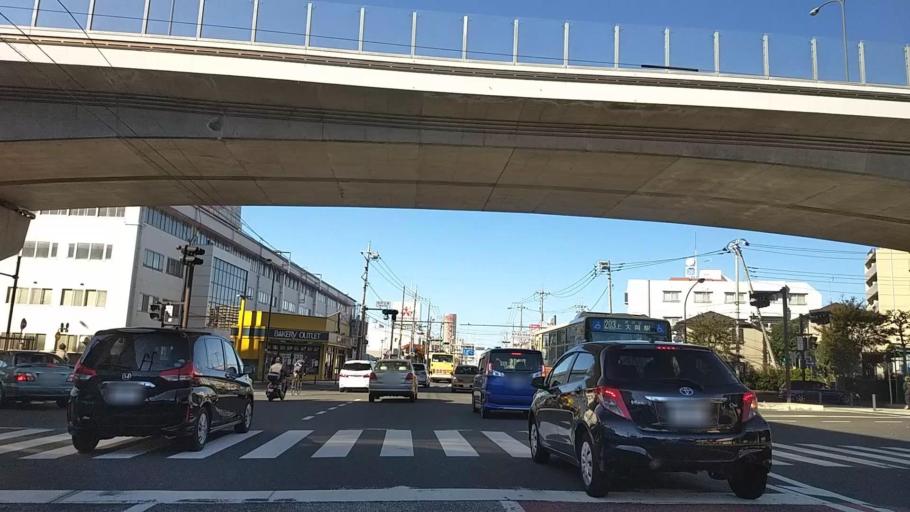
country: JP
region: Kanagawa
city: Yokohama
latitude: 35.4204
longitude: 139.5604
